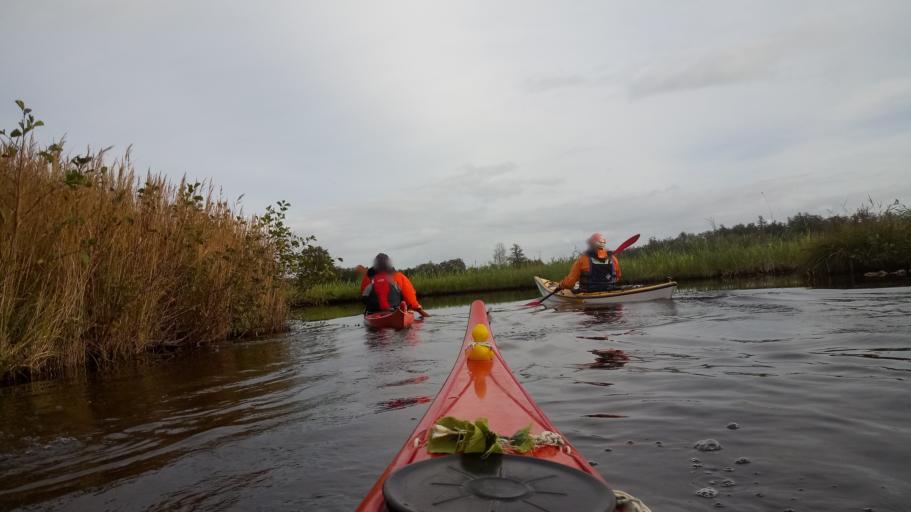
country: NL
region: Overijssel
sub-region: Gemeente Steenwijkerland
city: Sint Jansklooster
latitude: 52.6599
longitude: 6.0413
